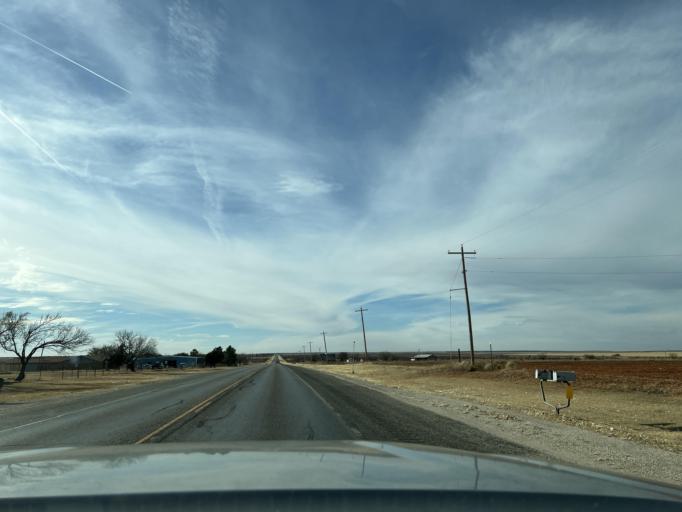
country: US
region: Texas
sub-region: Jones County
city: Anson
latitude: 32.7519
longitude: -99.9182
